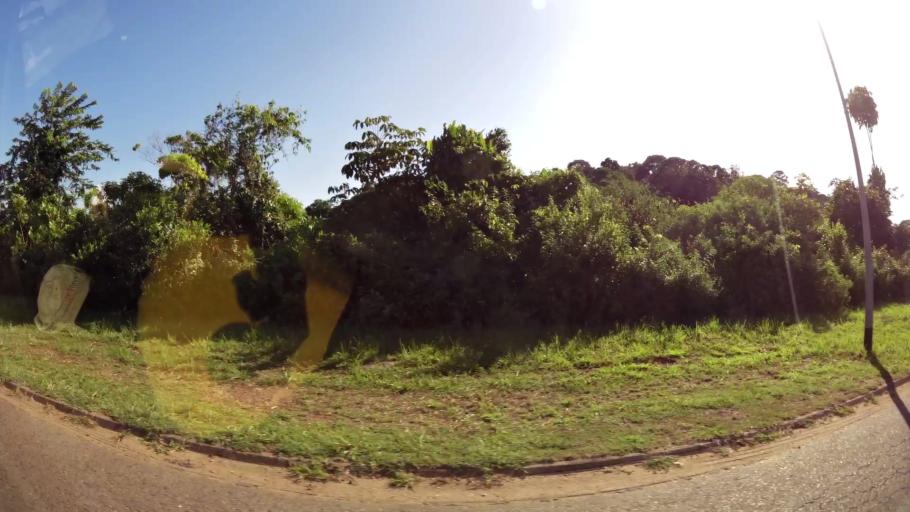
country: GF
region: Guyane
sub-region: Guyane
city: Matoury
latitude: 4.8615
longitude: -52.2766
